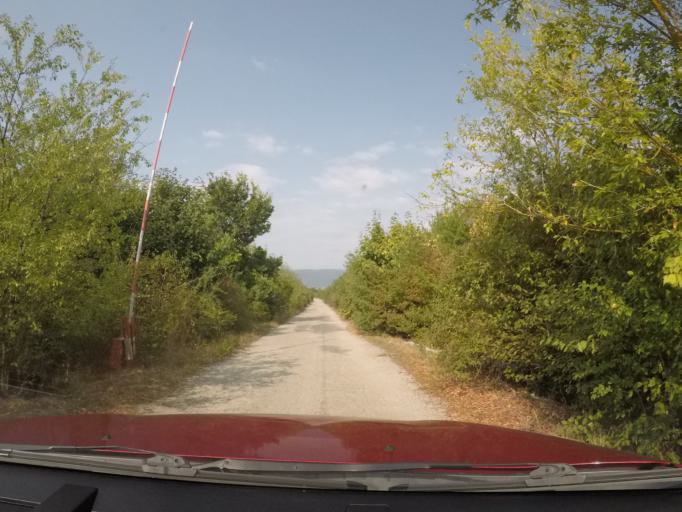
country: SK
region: Kosicky
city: Moldava nad Bodvou
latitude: 48.6062
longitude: 20.9505
